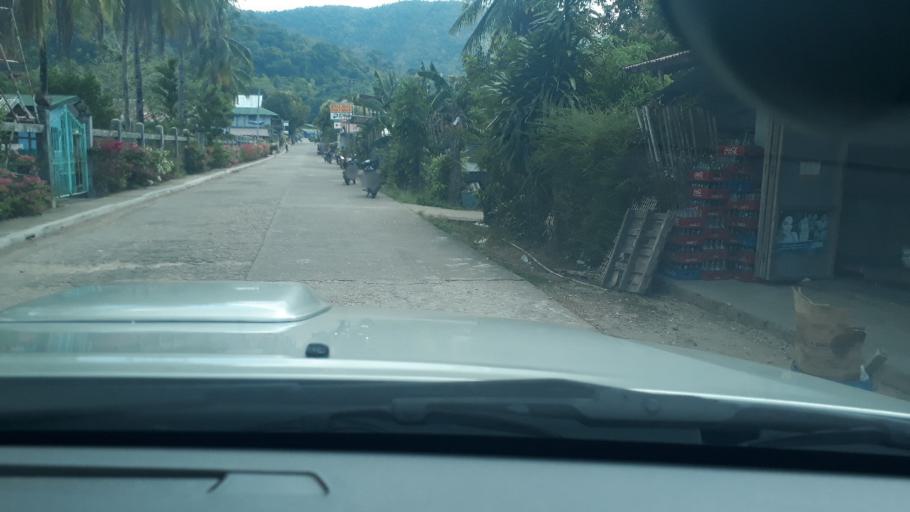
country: PH
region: Mimaropa
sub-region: Province of Palawan
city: Salvacion
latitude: 12.1318
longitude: 119.9347
